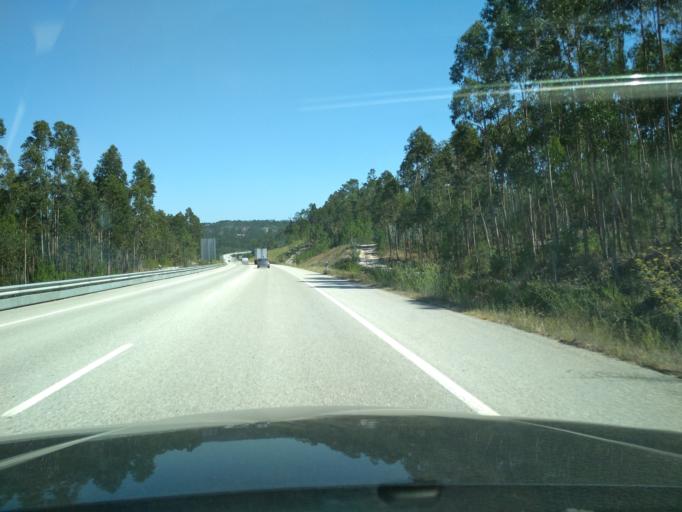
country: PT
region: Leiria
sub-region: Pombal
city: Lourical
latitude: 39.9809
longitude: -8.7192
